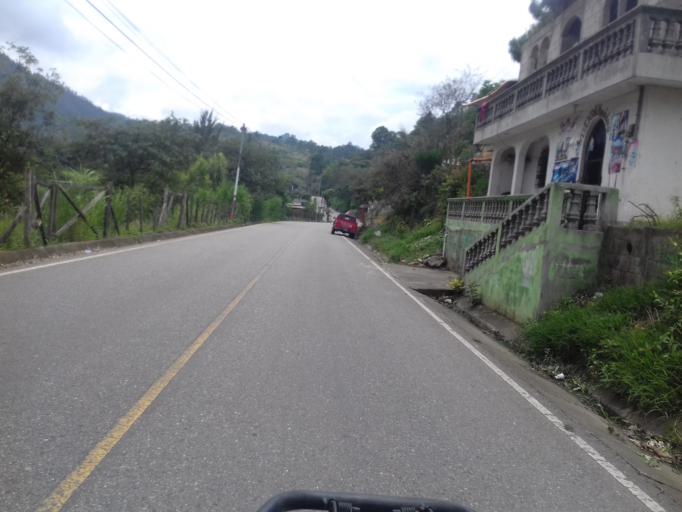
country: GT
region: Quiche
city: Uspantan
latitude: 15.3456
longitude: -90.8121
